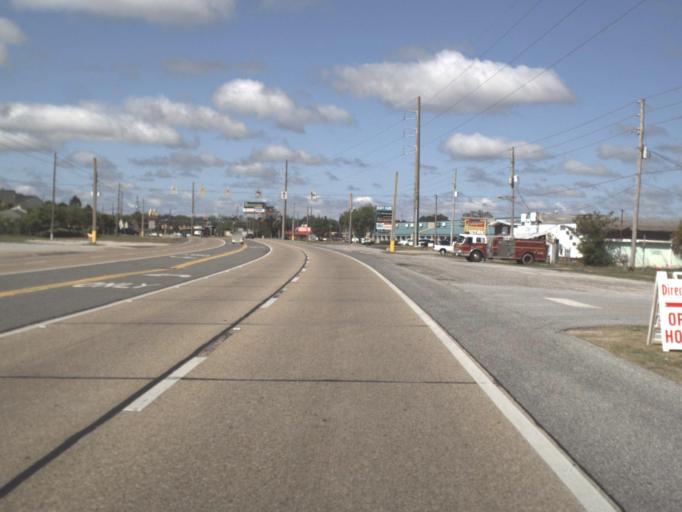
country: US
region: Florida
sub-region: Escambia County
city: West Pensacola
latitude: 30.4091
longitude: -87.2702
